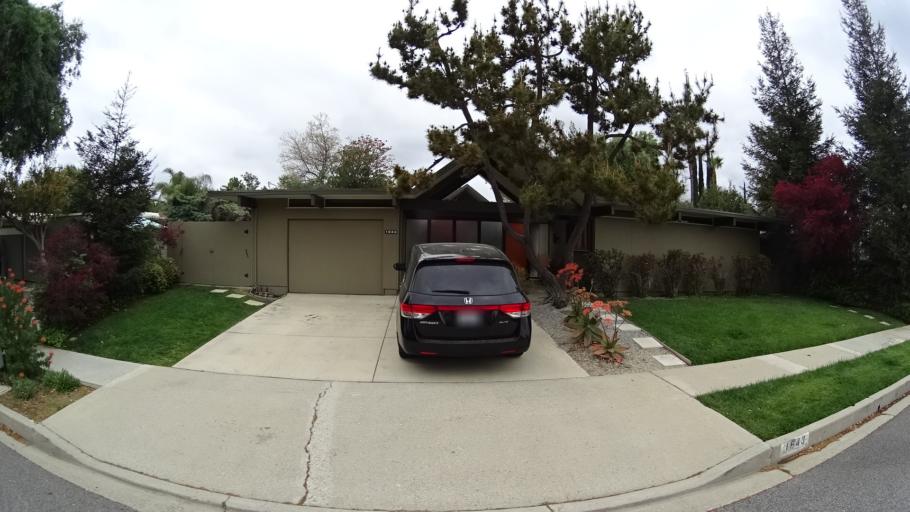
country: US
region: California
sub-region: Ventura County
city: Casa Conejo
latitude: 34.2009
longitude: -118.8886
